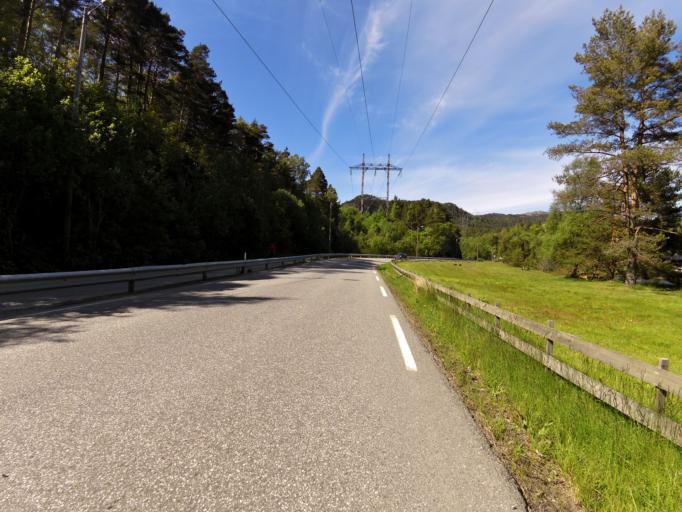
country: NO
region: Hordaland
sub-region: Stord
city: Sagvag
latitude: 59.7854
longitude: 5.4147
